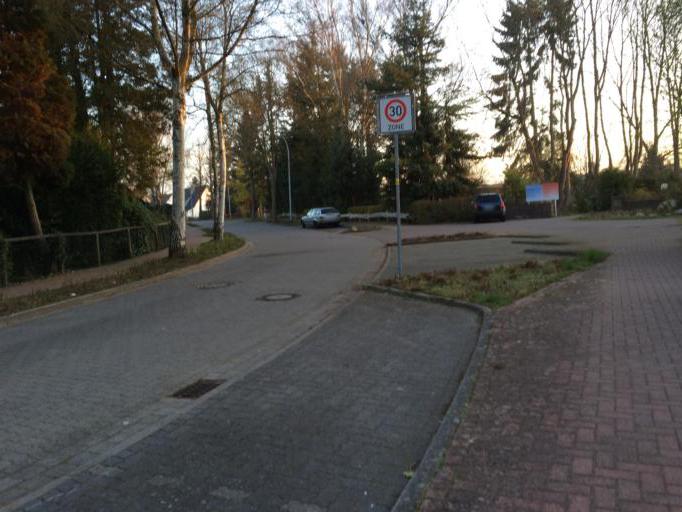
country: DE
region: Lower Saxony
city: Walsrode
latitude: 52.8635
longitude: 9.5819
